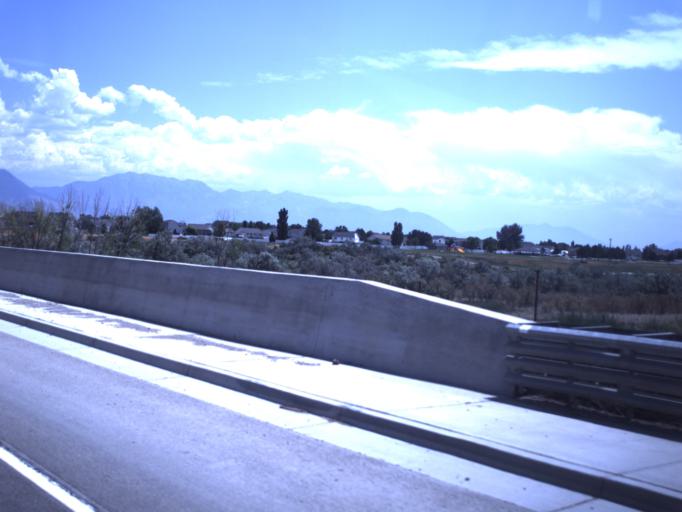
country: US
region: Utah
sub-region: Utah County
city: Lehi
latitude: 40.4124
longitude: -111.9010
